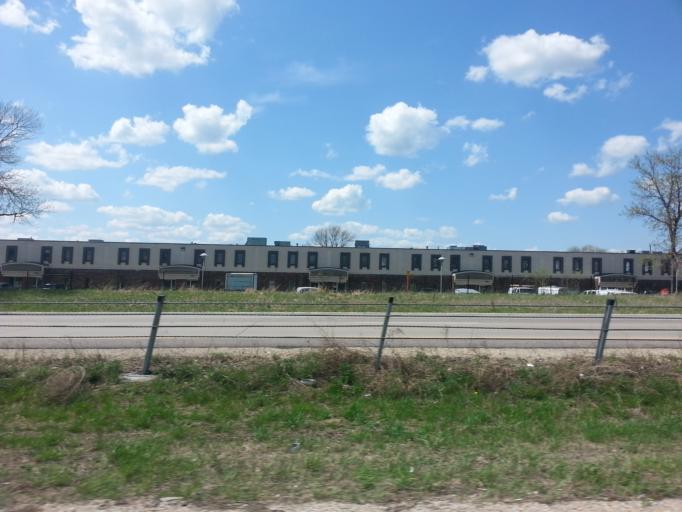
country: US
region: Minnesota
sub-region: Hennepin County
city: Edina
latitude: 44.8679
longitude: -93.3968
